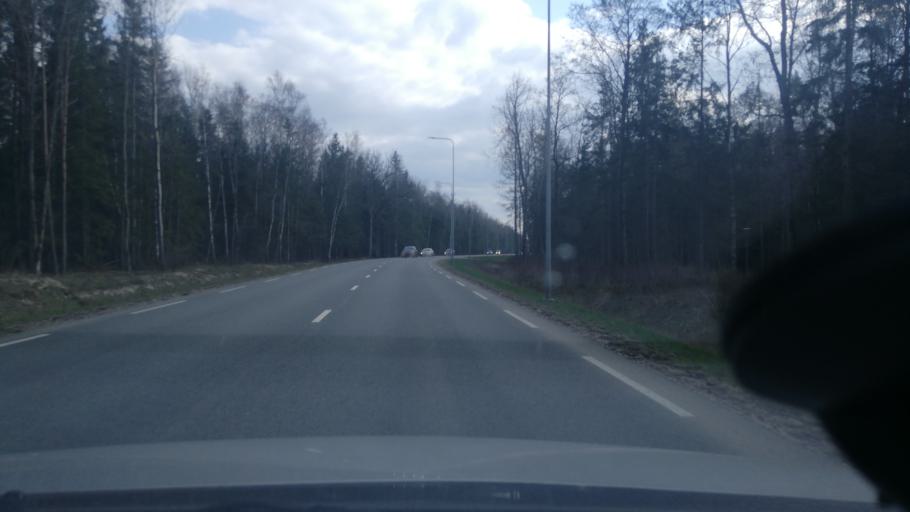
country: LT
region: Klaipedos apskritis
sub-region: Klaipeda
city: Klaipeda
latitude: 55.7524
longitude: 21.0910
